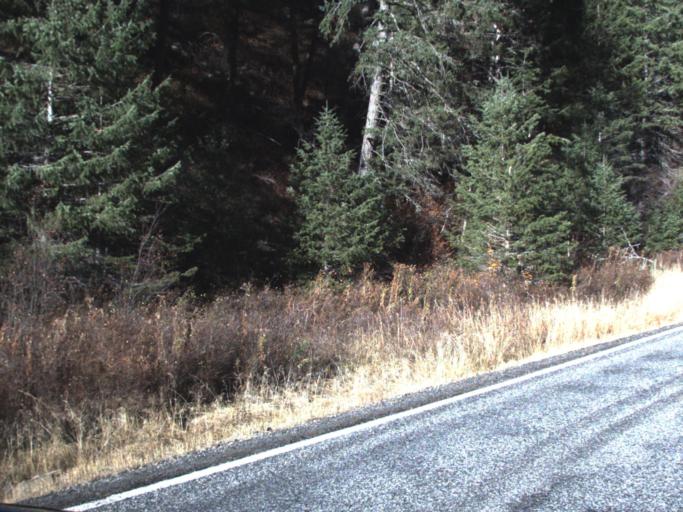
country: US
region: Washington
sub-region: Ferry County
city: Republic
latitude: 48.5369
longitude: -118.7399
